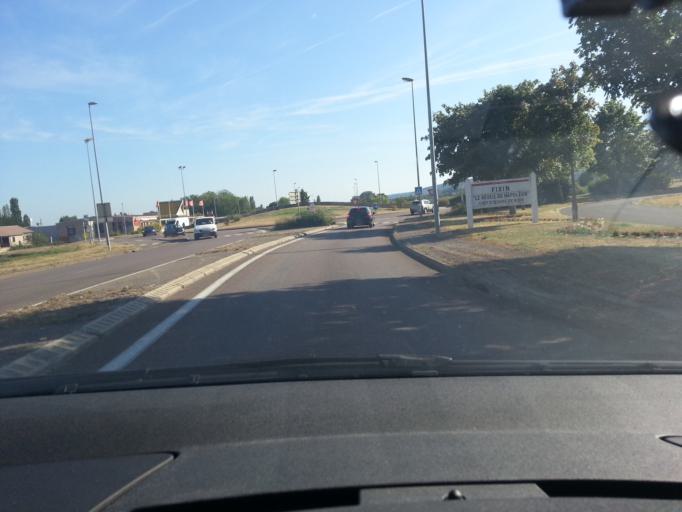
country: FR
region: Bourgogne
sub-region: Departement de la Cote-d'Or
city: Couchey
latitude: 47.2447
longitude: 4.9881
